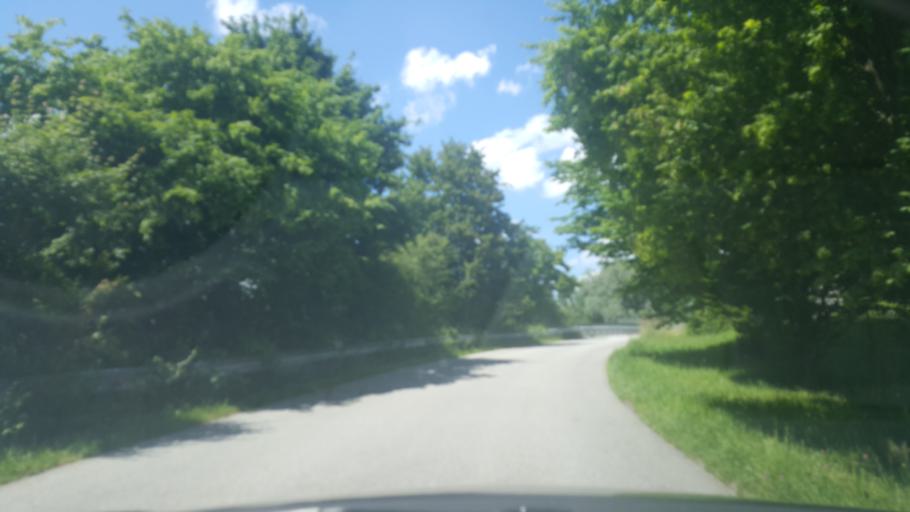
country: AT
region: Upper Austria
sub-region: Politischer Bezirk Vocklabruck
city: Seewalchen
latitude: 47.9574
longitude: 13.5761
